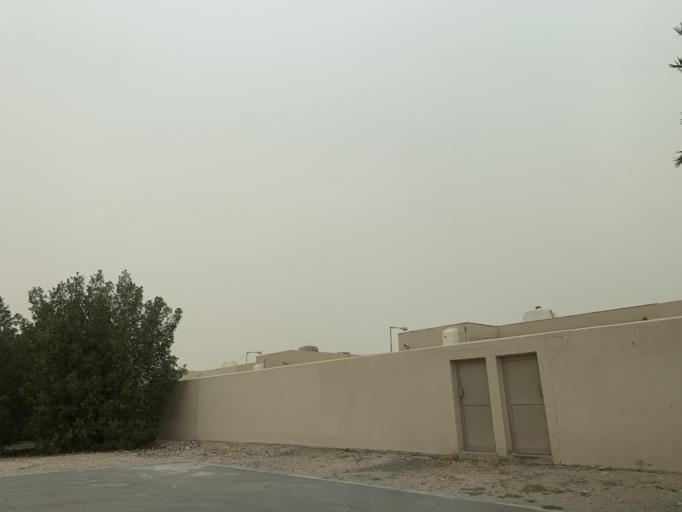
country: BH
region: Central Governorate
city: Madinat Hamad
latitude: 26.1322
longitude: 50.5257
